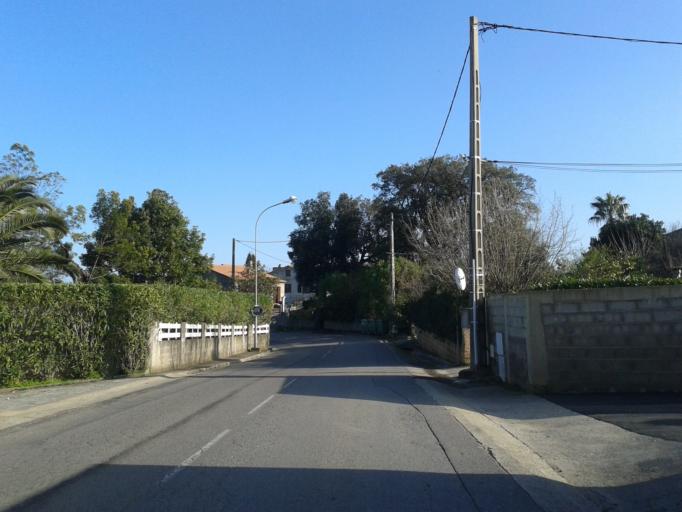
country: FR
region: Corsica
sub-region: Departement de la Haute-Corse
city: Biguglia
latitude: 42.5917
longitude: 9.4274
